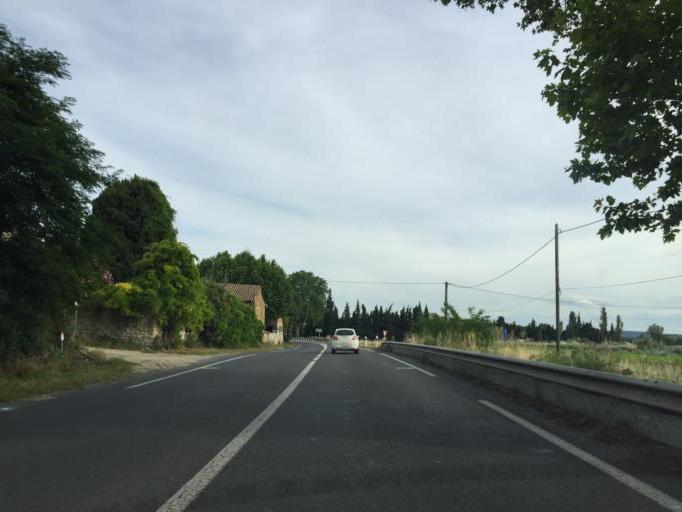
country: FR
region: Provence-Alpes-Cote d'Azur
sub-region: Departement du Vaucluse
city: Mondragon
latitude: 44.2253
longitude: 4.7143
